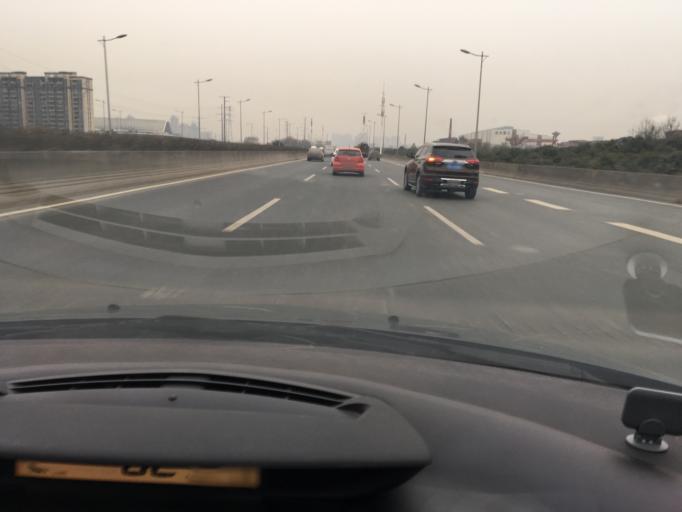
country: CN
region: Hubei
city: Hongqi
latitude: 30.6013
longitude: 114.4265
